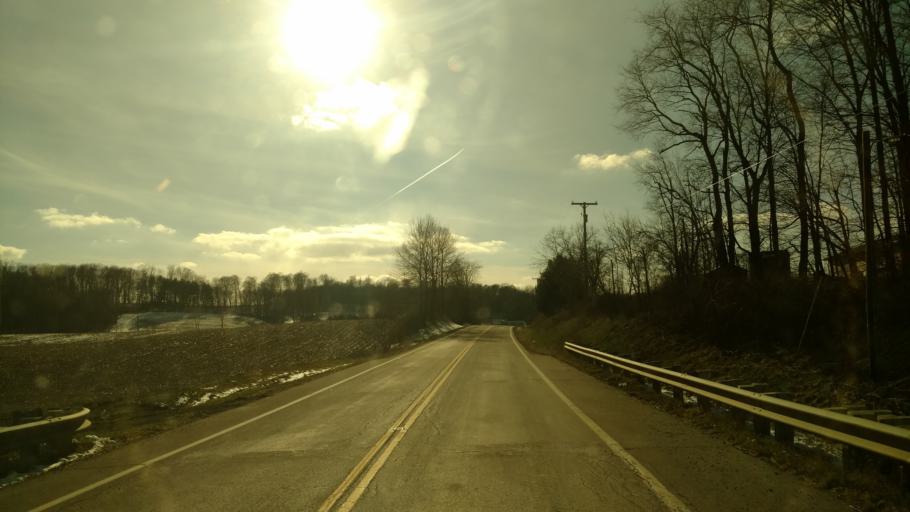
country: US
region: Ohio
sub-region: Ashland County
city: Loudonville
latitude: 40.6785
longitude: -82.2830
